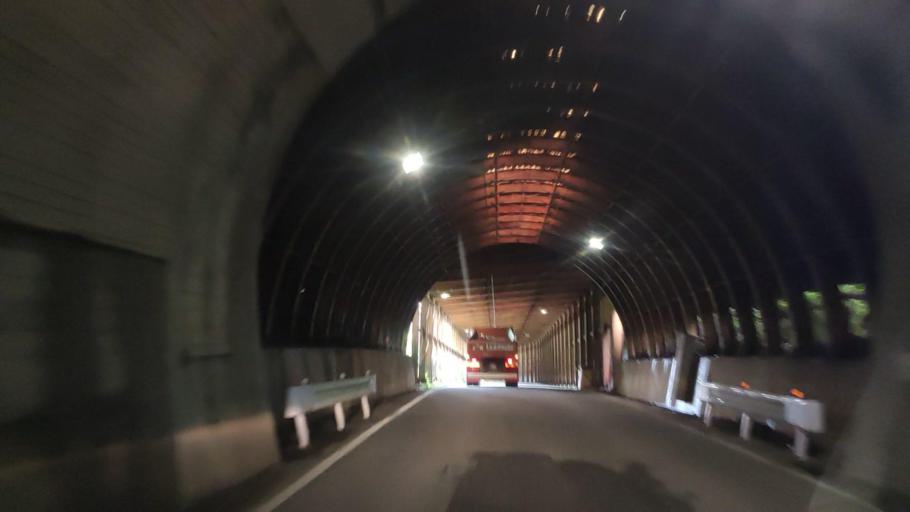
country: JP
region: Nagano
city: Iiyama
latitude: 36.8759
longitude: 138.3197
